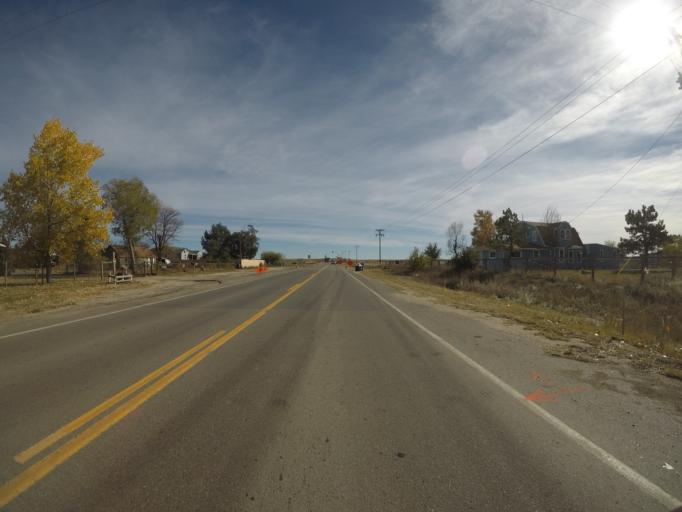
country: US
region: Colorado
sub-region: Adams County
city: Strasburg
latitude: 39.7384
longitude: -104.3187
